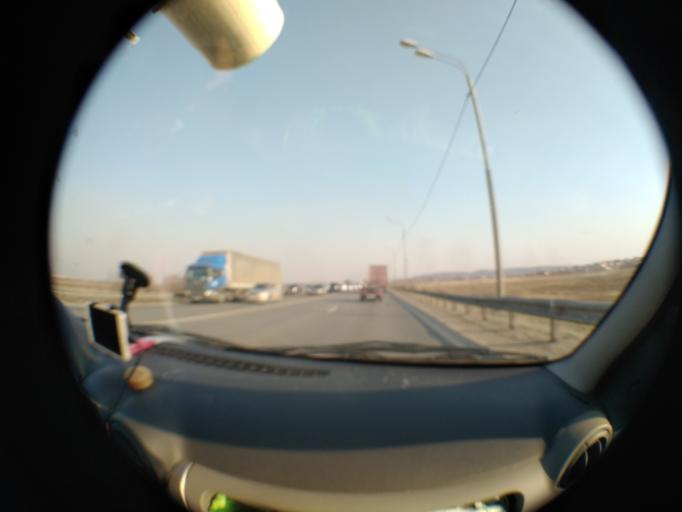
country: RU
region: Moskovskaya
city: Ostrovtsy
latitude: 55.5807
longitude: 38.0166
